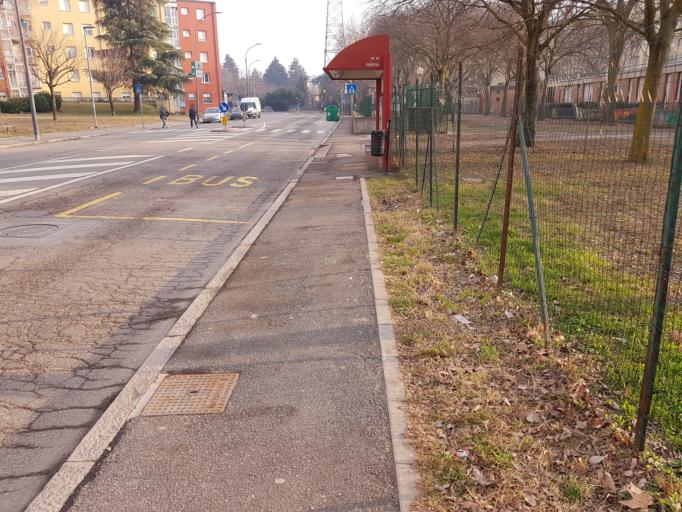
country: IT
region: Emilia-Romagna
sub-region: Provincia di Bologna
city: Quarto Inferiore
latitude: 44.5094
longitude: 11.3932
